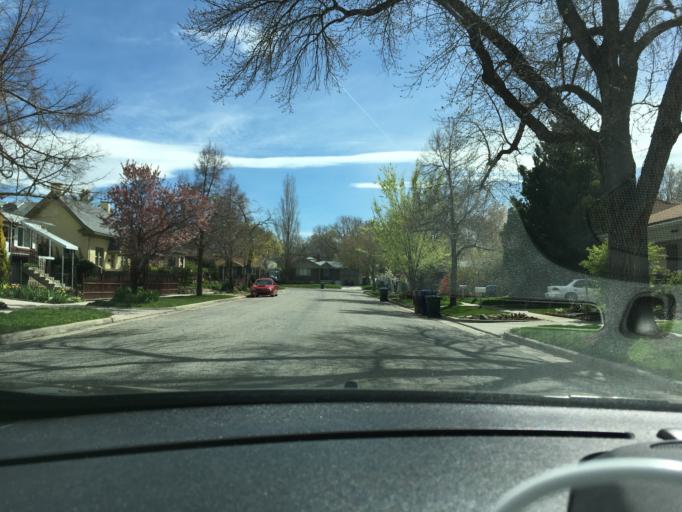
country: US
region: Utah
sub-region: Salt Lake County
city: South Salt Lake
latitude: 40.7369
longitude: -111.8639
